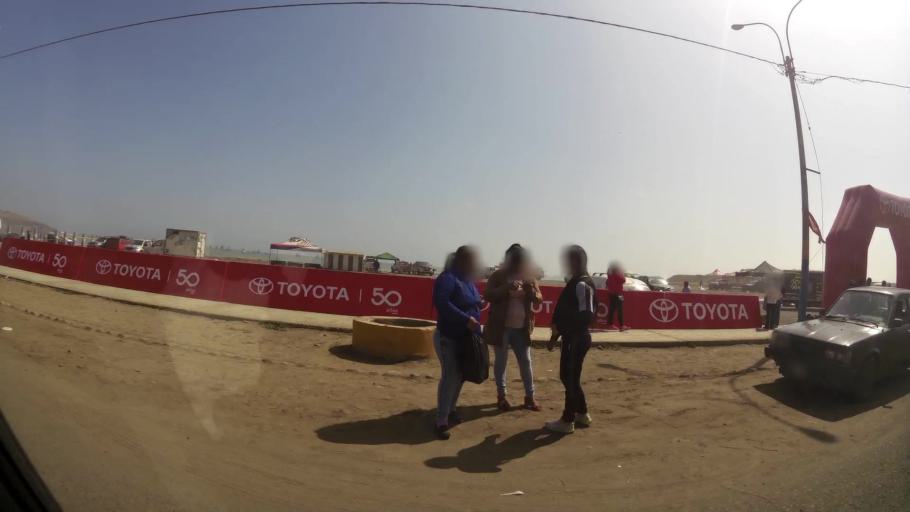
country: PE
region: Lima
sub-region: Huaura
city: Huacho
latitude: -11.1105
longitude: -77.6142
